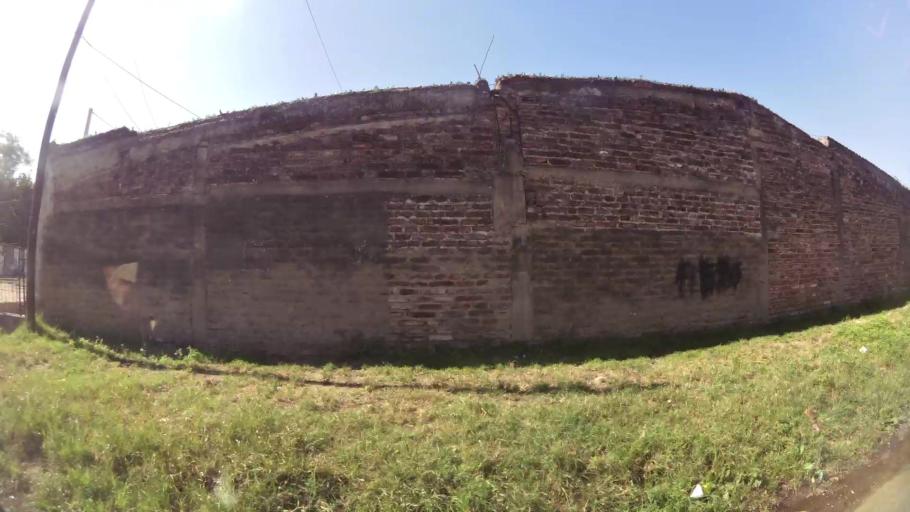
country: AR
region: Cordoba
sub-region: Departamento de Capital
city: Cordoba
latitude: -31.4098
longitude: -64.1463
